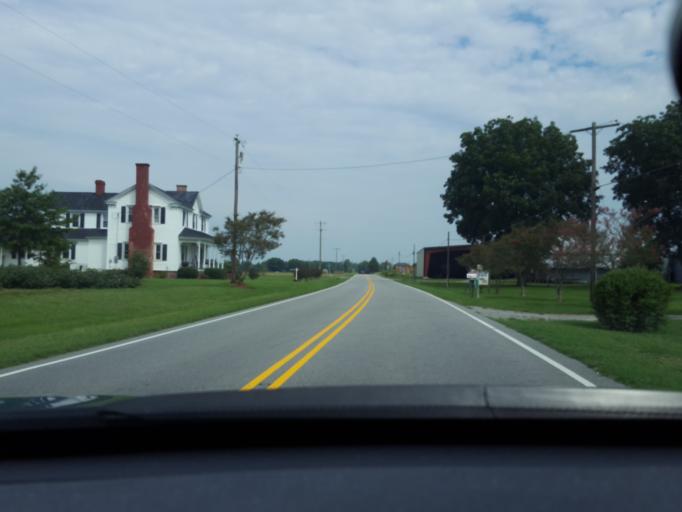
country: US
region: North Carolina
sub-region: Chowan County
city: Edenton
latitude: 36.1901
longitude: -76.6610
